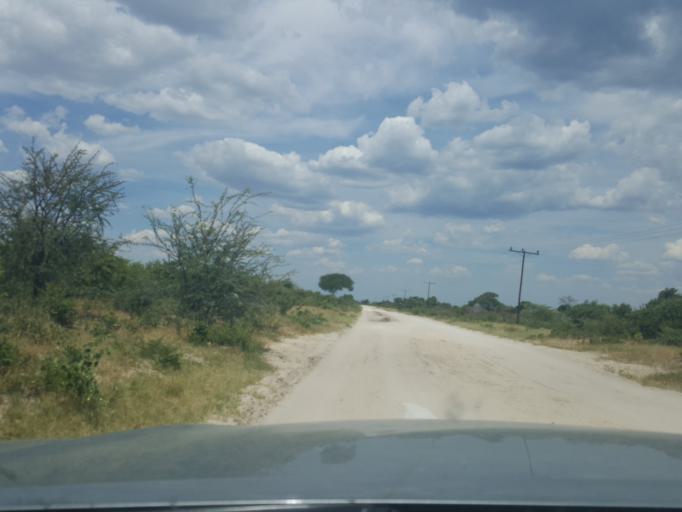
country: BW
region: North West
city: Shakawe
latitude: -18.5046
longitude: 22.1363
